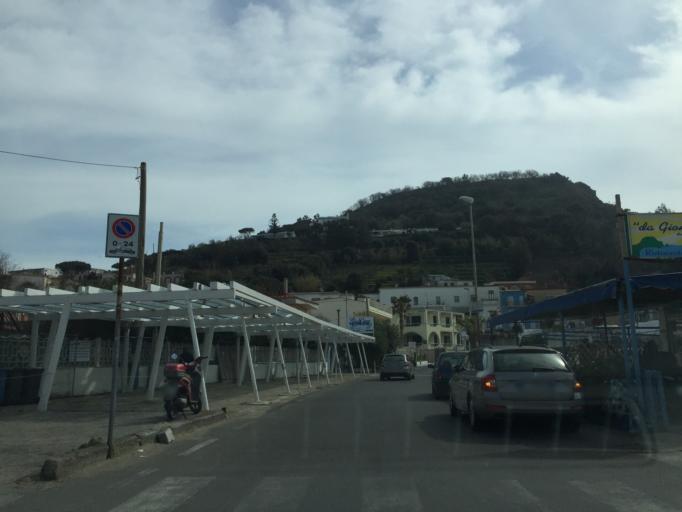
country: IT
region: Campania
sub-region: Provincia di Napoli
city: Bacoli
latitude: 40.7860
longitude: 14.0841
